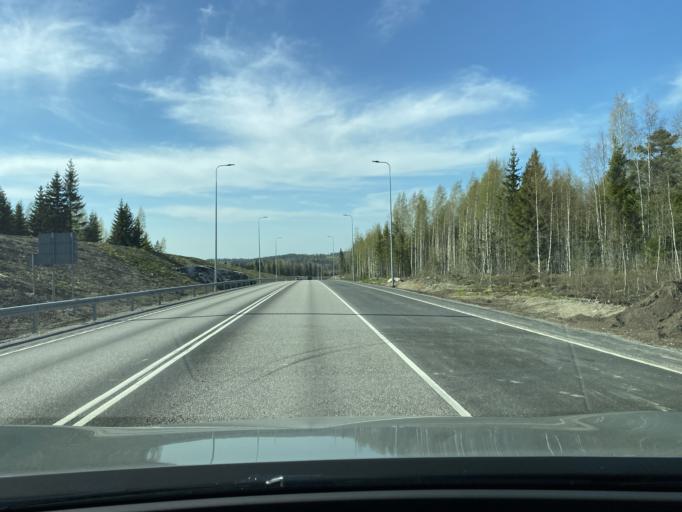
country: FI
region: Uusimaa
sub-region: Helsinki
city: Nurmijaervi
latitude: 60.3902
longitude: 24.7827
